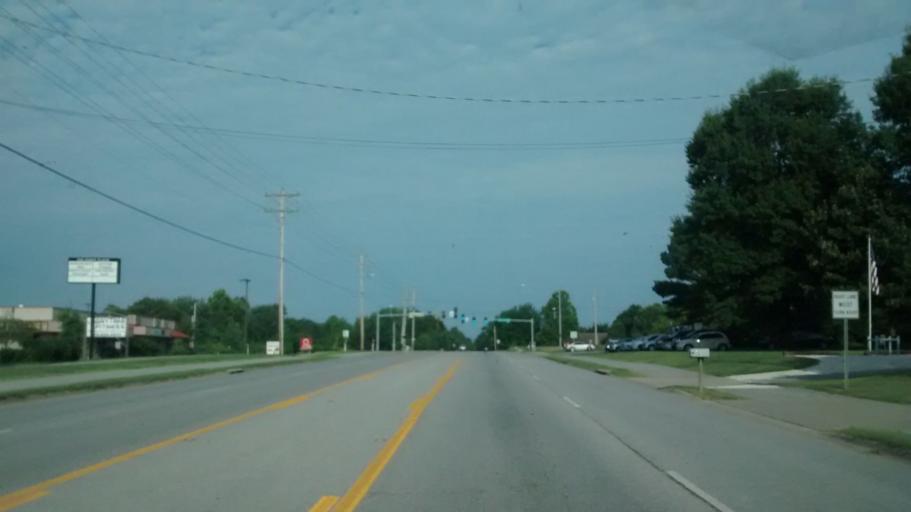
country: US
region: Arkansas
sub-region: Washington County
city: Farmington
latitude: 36.0793
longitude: -94.2512
